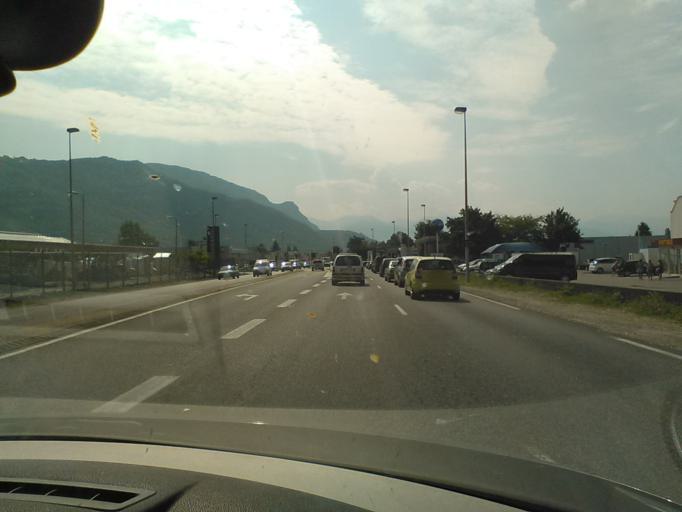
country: FR
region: Rhone-Alpes
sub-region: Departement de la Savoie
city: La Ravoire
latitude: 45.5660
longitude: 5.9661
